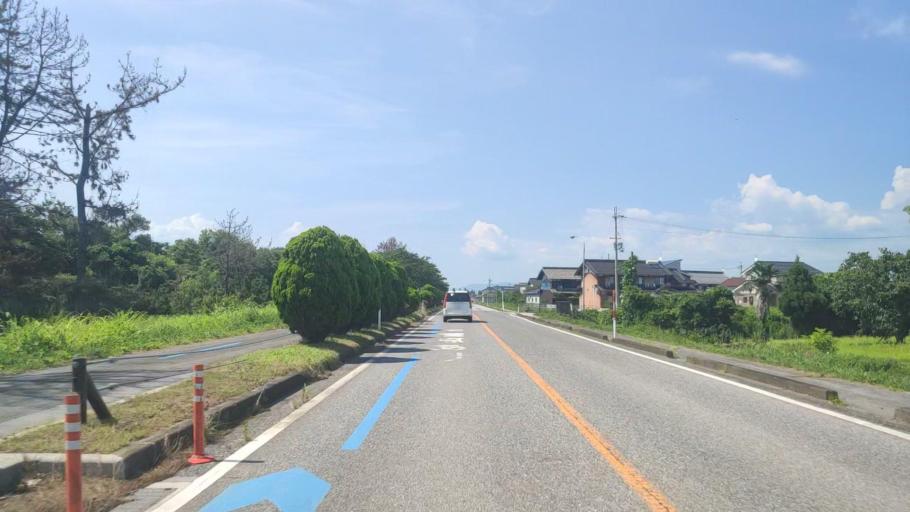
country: JP
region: Shiga Prefecture
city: Nagahama
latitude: 35.4002
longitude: 136.2166
